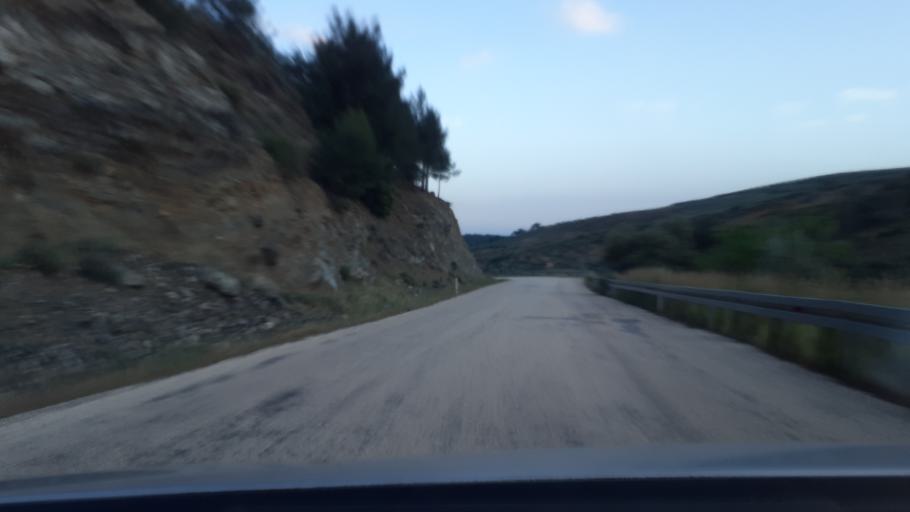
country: TR
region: Hatay
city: Kirikhan
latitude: 36.5170
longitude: 36.3186
